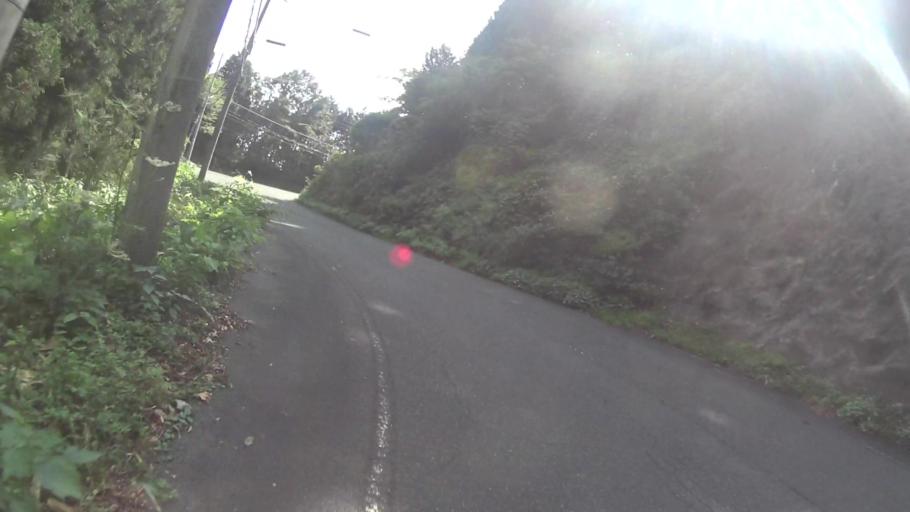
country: JP
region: Kyoto
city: Miyazu
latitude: 35.7145
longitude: 135.1940
